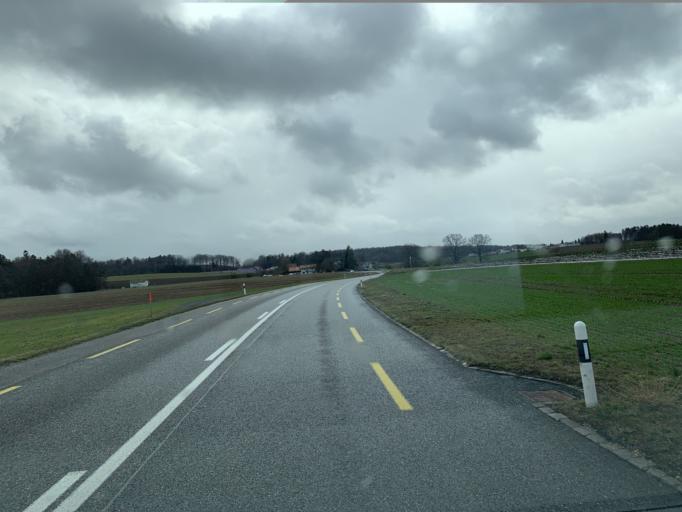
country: CH
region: Fribourg
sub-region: Sense District
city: Dudingen
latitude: 46.8685
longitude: 7.1961
